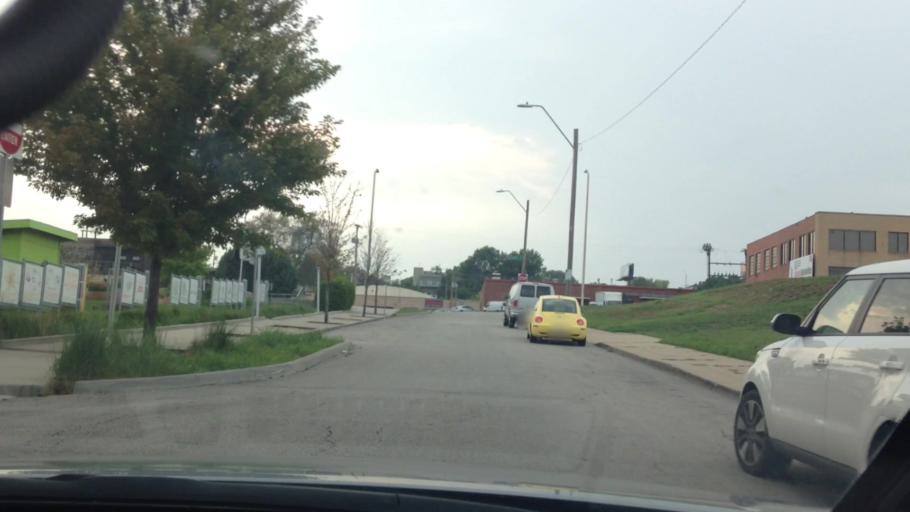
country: US
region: Missouri
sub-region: Jackson County
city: Kansas City
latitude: 39.0920
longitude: -94.5877
